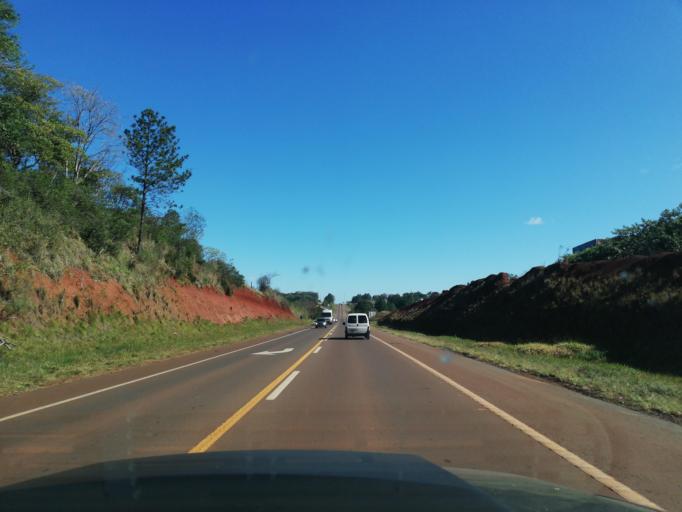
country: AR
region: Misiones
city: Aristobulo del Valle
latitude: -27.0901
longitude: -54.8624
